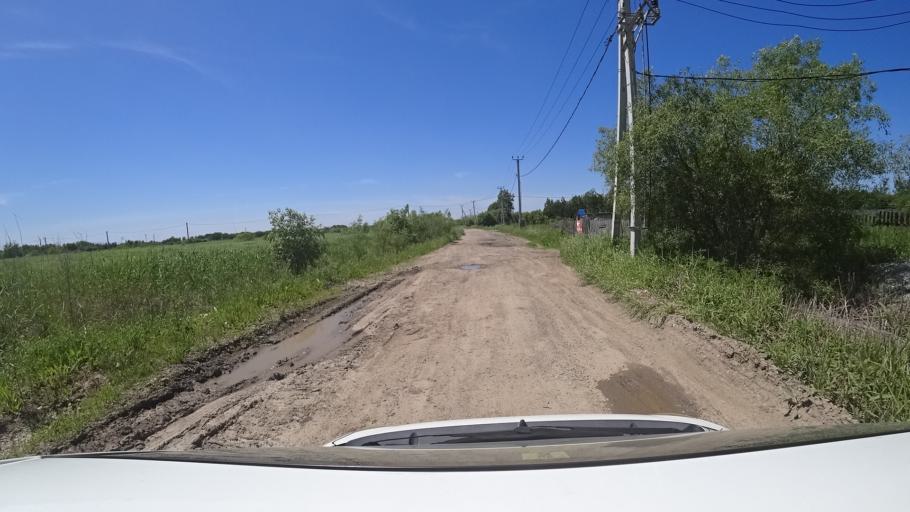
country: RU
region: Khabarovsk Krai
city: Topolevo
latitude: 48.5004
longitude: 135.1964
